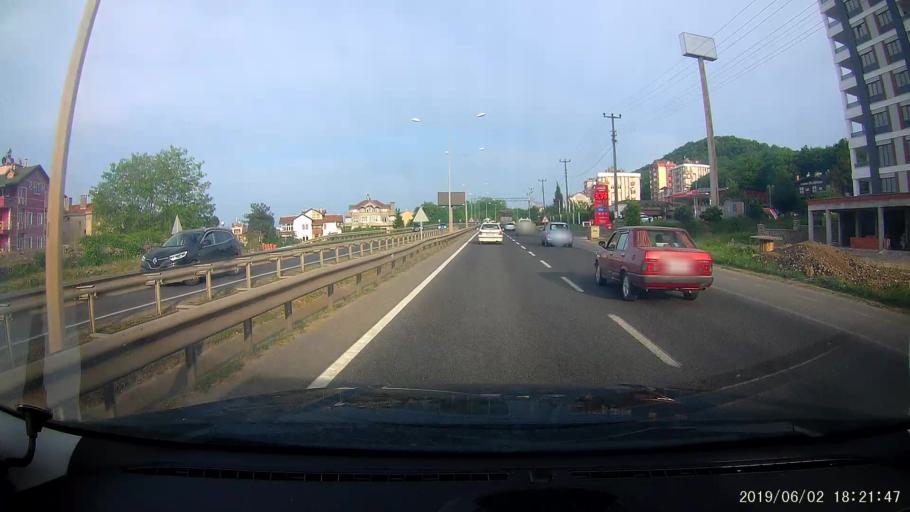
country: TR
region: Ordu
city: Fatsa
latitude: 41.0621
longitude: 37.4721
